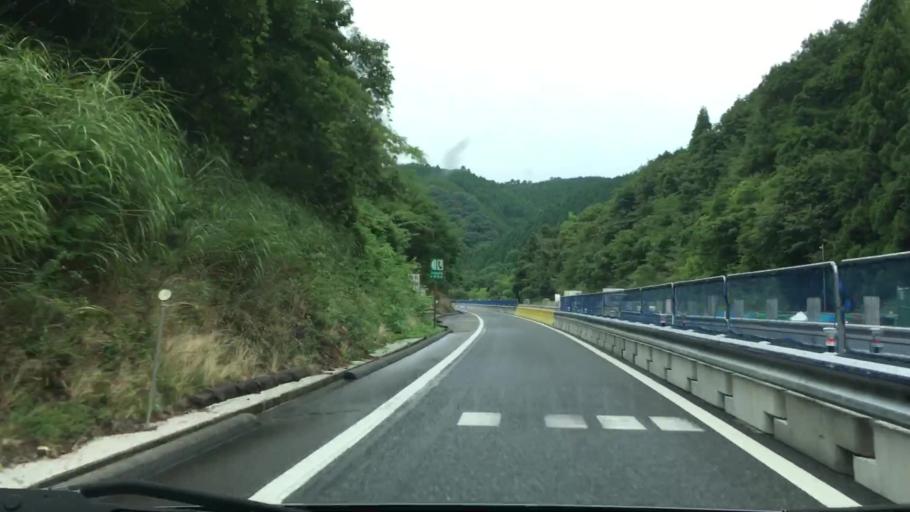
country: JP
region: Okayama
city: Niimi
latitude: 35.0329
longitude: 133.5753
